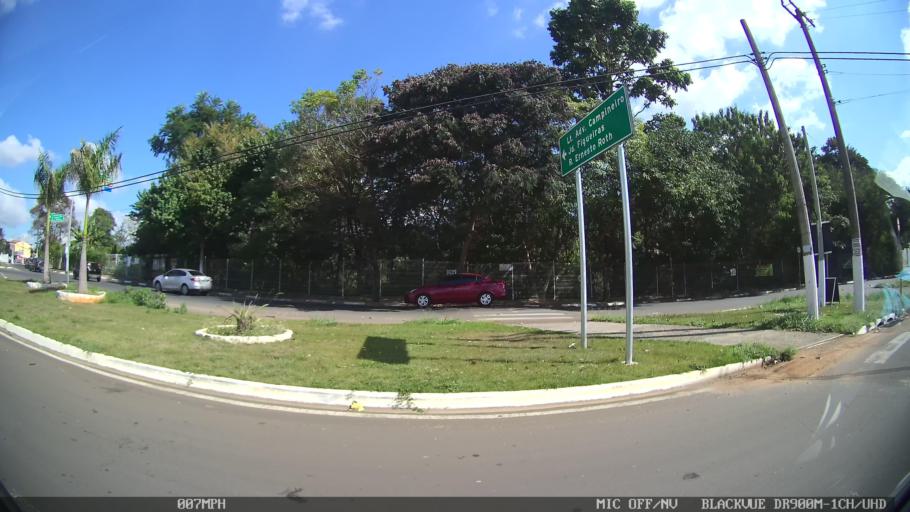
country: BR
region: Sao Paulo
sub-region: Hortolandia
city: Hortolandia
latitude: -22.8813
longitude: -47.2222
